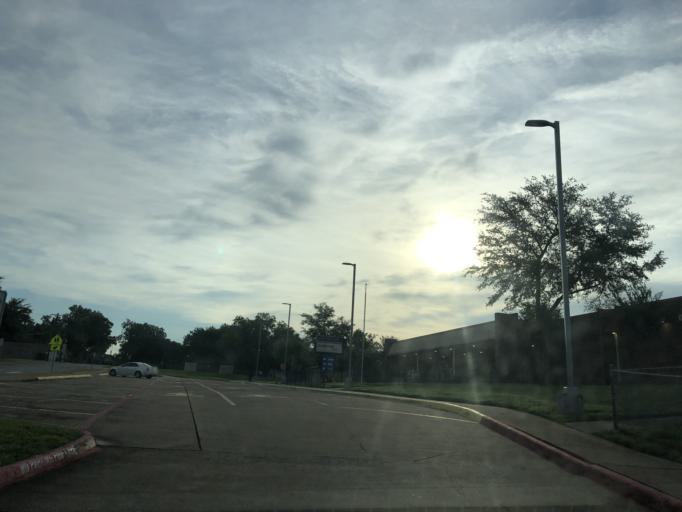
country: US
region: Texas
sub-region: Dallas County
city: Rowlett
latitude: 32.8501
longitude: -96.6068
